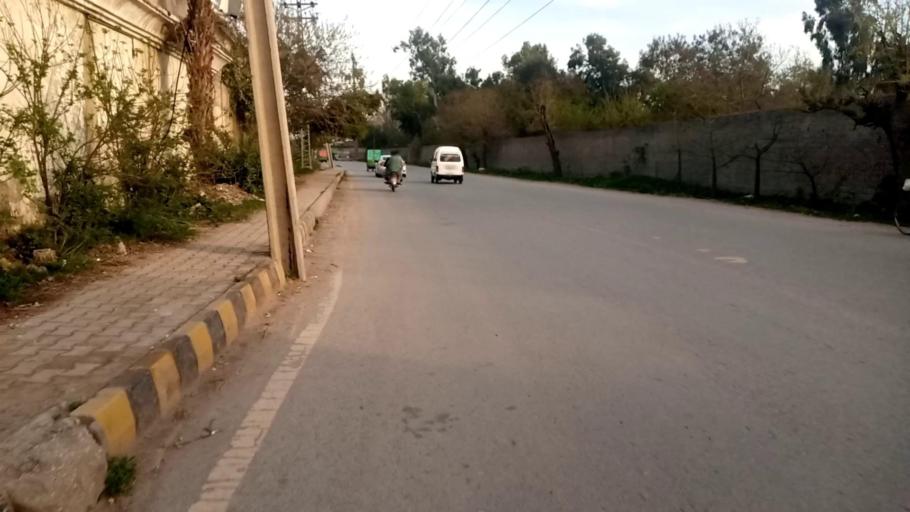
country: PK
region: Khyber Pakhtunkhwa
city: Peshawar
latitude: 34.0206
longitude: 71.5650
